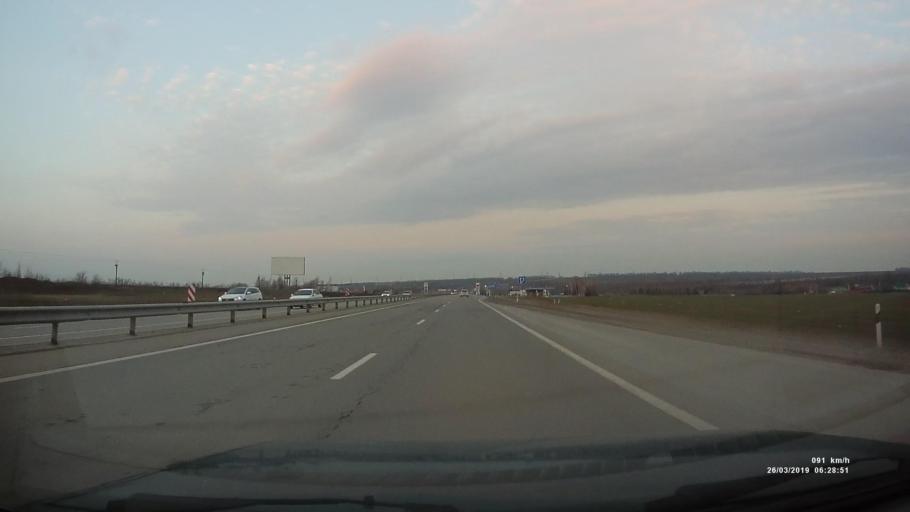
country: RU
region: Rostov
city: Krym
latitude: 47.2662
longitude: 39.5849
